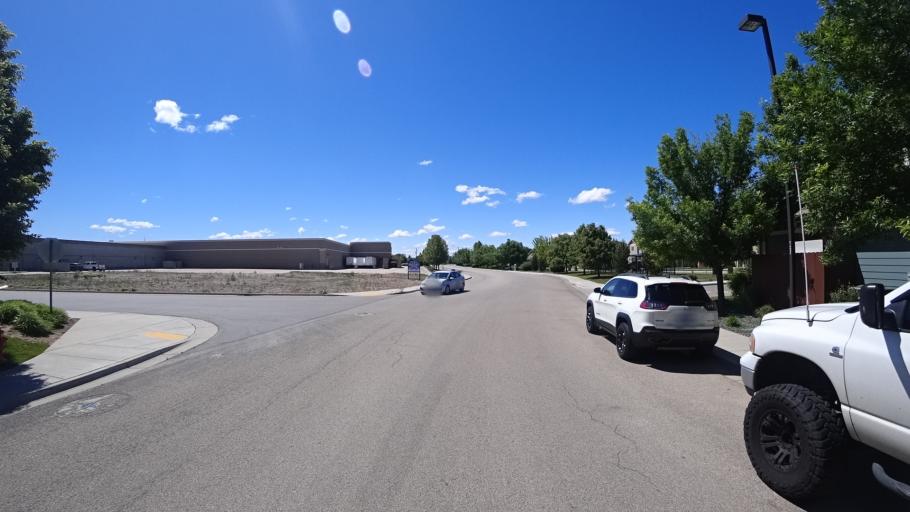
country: US
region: Idaho
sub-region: Ada County
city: Meridian
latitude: 43.6359
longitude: -116.3587
